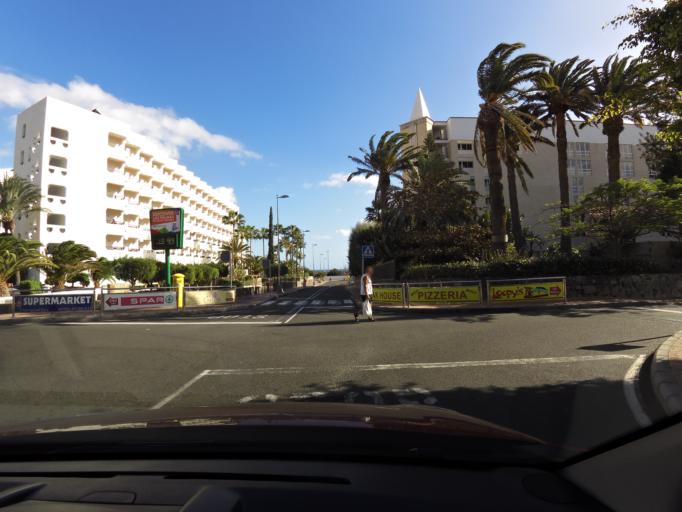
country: ES
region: Canary Islands
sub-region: Provincia de Las Palmas
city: Playa del Ingles
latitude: 27.7722
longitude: -15.5412
